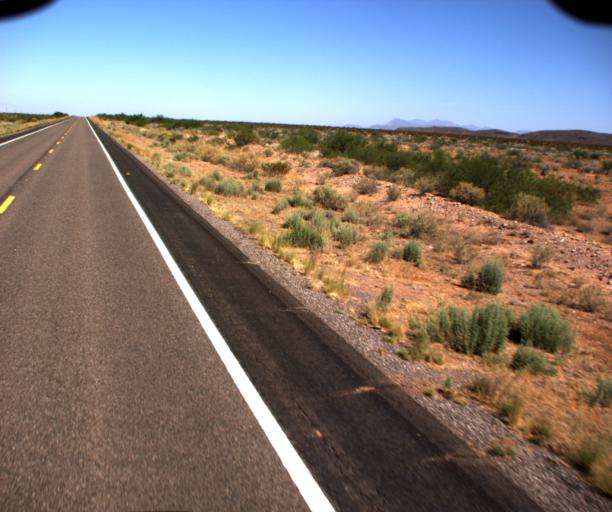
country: US
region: Arizona
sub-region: Graham County
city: Swift Trail Junction
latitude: 32.7550
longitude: -109.4211
